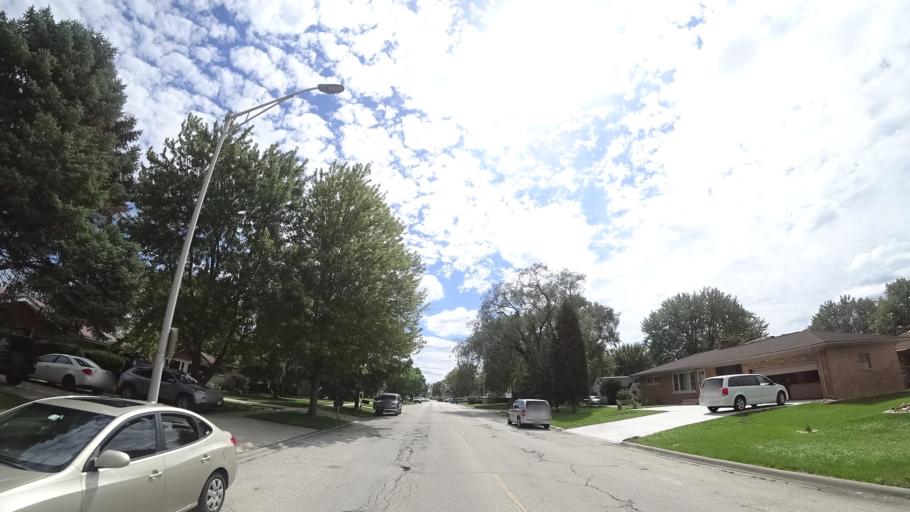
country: US
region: Illinois
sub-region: Cook County
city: Chicago Ridge
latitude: 41.7153
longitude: -87.7895
